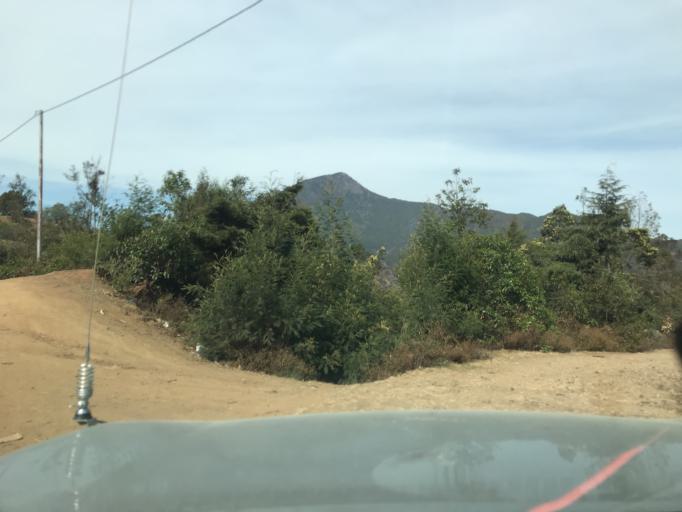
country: TL
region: Ainaro
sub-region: Ainaro
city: Ainaro
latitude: -8.8853
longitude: 125.5347
